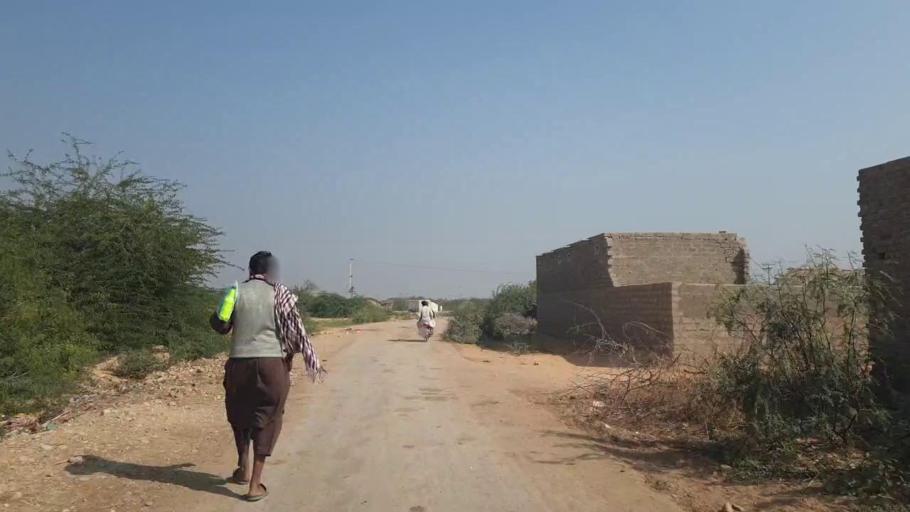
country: PK
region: Sindh
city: Matiari
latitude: 25.5412
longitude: 68.3487
